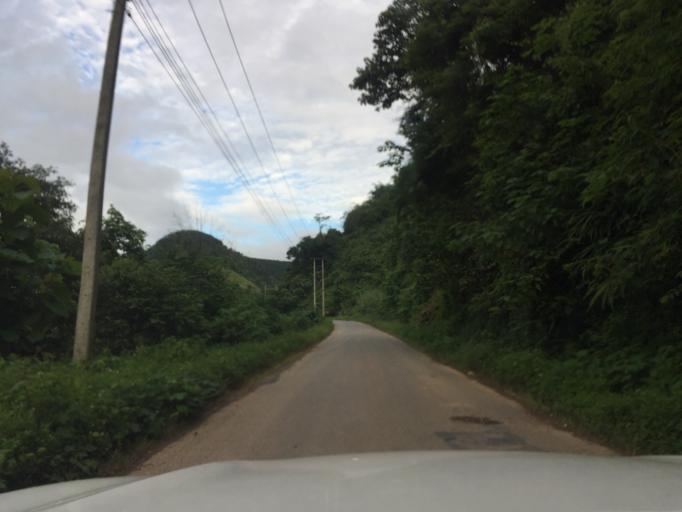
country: LA
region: Phongsali
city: Khoa
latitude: 21.1038
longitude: 102.3012
